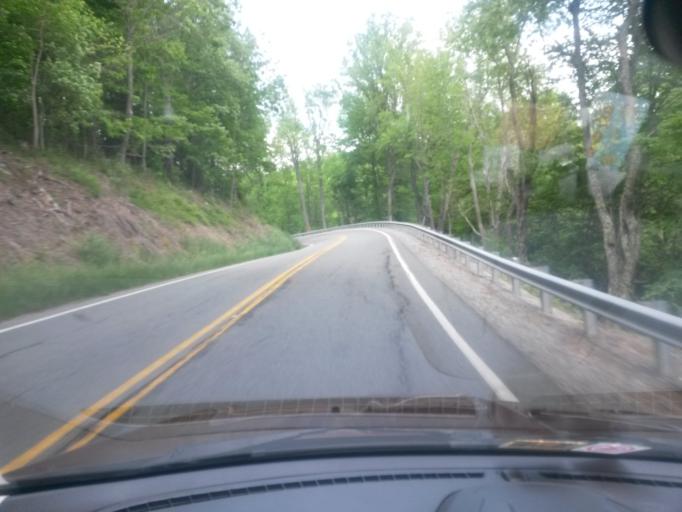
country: US
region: Virginia
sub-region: Floyd County
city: Floyd
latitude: 36.8781
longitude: -80.3302
